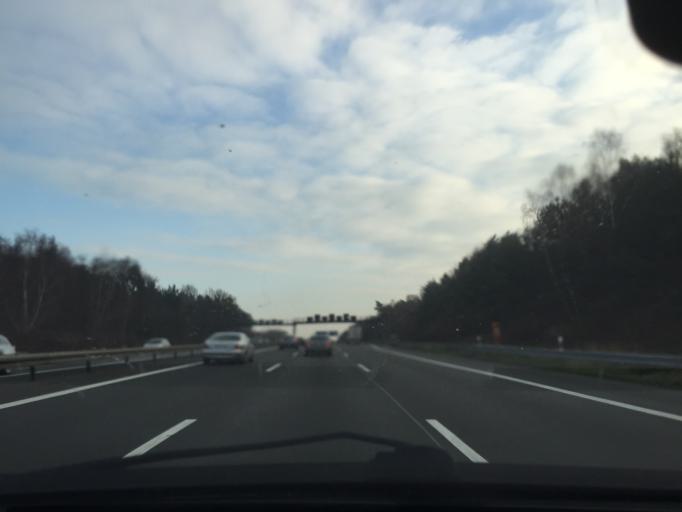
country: DE
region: Brandenburg
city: Fichtenwalde
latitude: 52.2987
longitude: 12.8994
